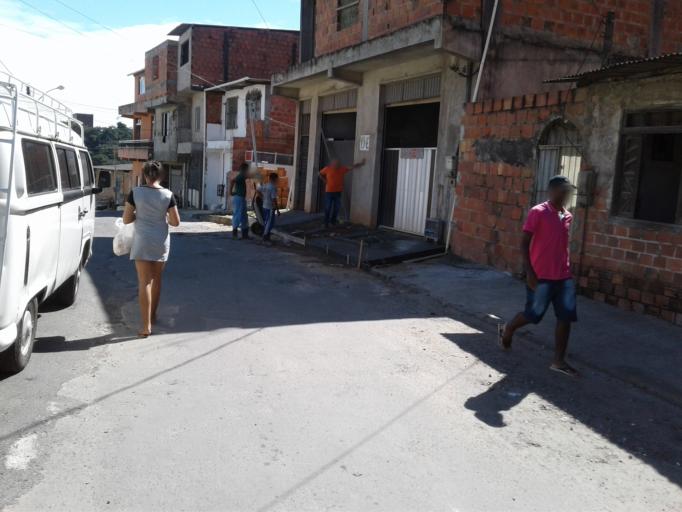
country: BR
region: Bahia
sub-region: Salvador
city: Salvador
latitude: -12.9131
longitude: -38.4660
